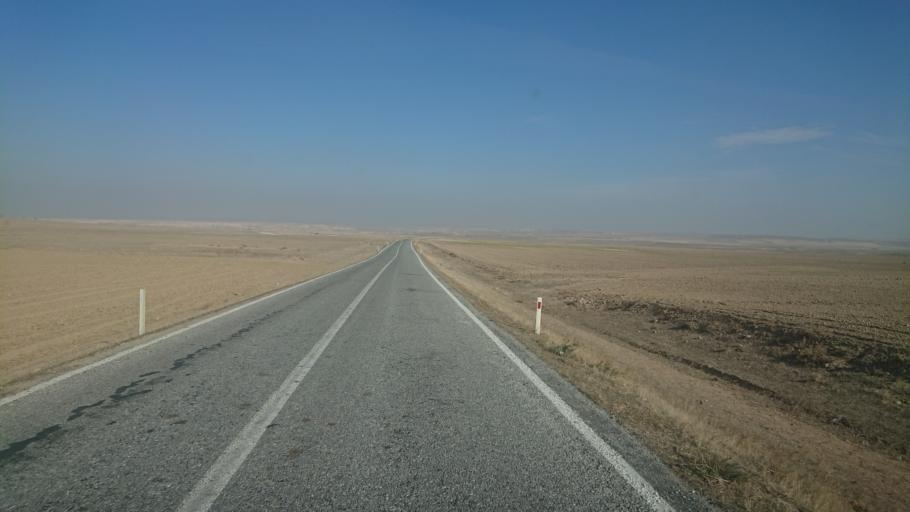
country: TR
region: Aksaray
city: Sultanhani
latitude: 38.0339
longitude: 33.5763
